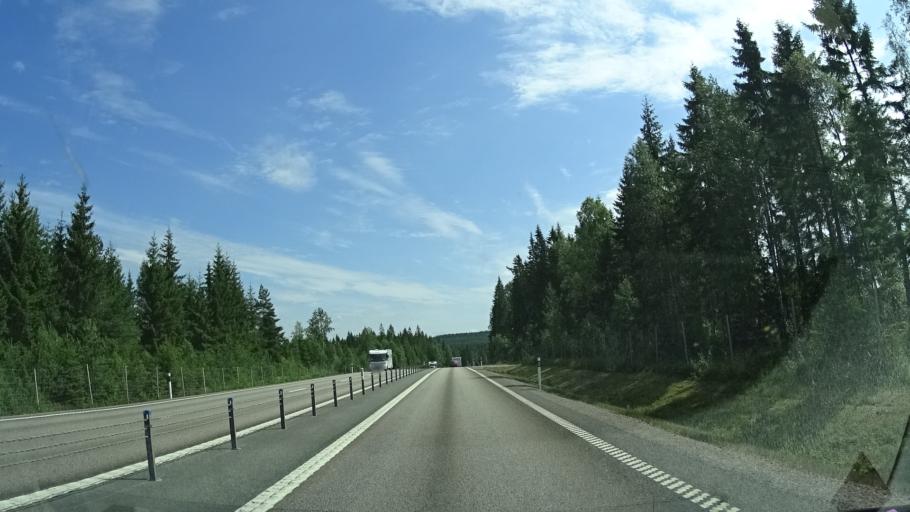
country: SE
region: Vaermland
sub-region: Kristinehamns Kommun
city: Bjorneborg
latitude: 59.3125
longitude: 14.2519
